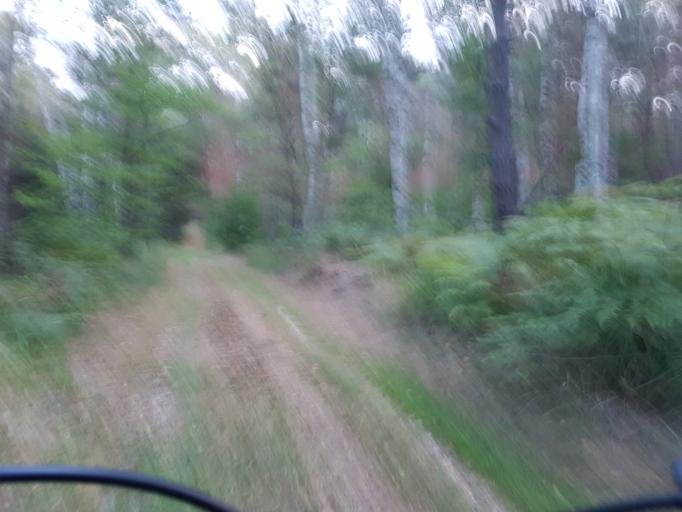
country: DE
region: Brandenburg
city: Trobitz
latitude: 51.5666
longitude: 13.4527
